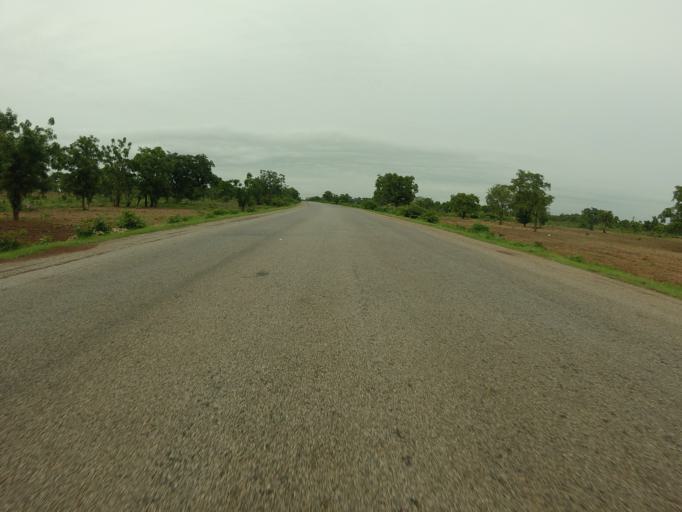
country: GH
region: Northern
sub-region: Yendi
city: Yendi
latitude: 9.5168
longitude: -0.0289
